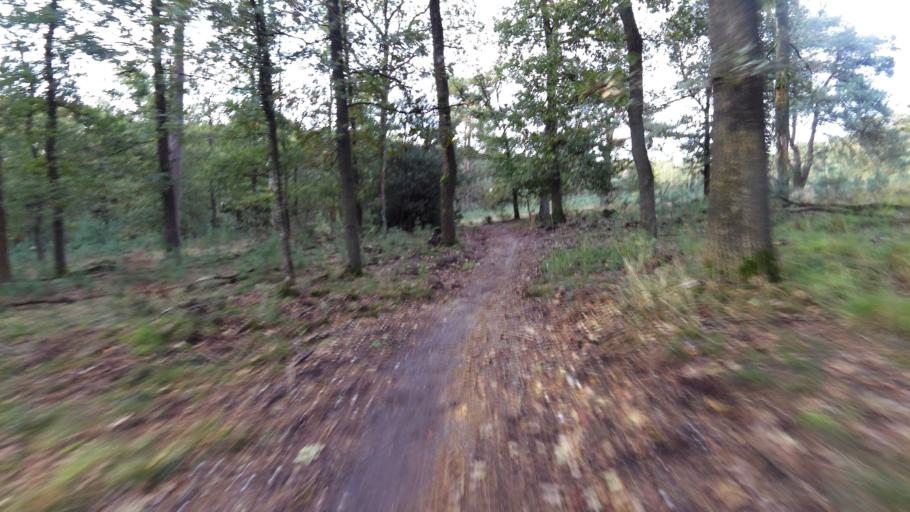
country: NL
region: Gelderland
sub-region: Gemeente Renkum
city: Wolfheze
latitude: 52.0268
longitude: 5.8171
